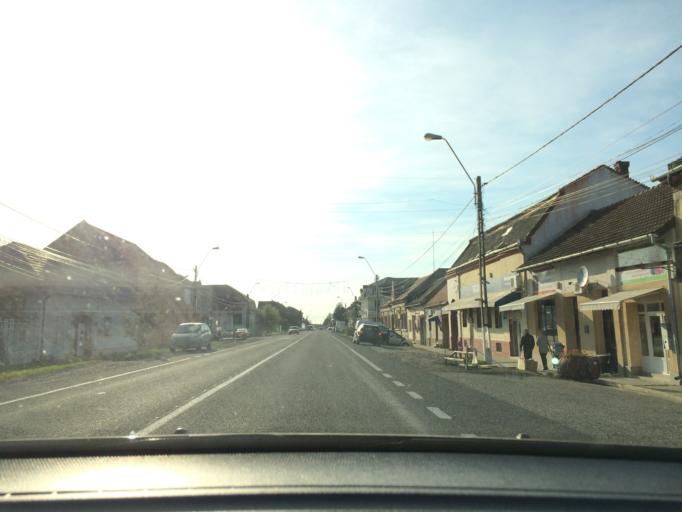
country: RO
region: Timis
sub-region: Oras Recas
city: Recas
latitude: 45.7997
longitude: 21.5072
